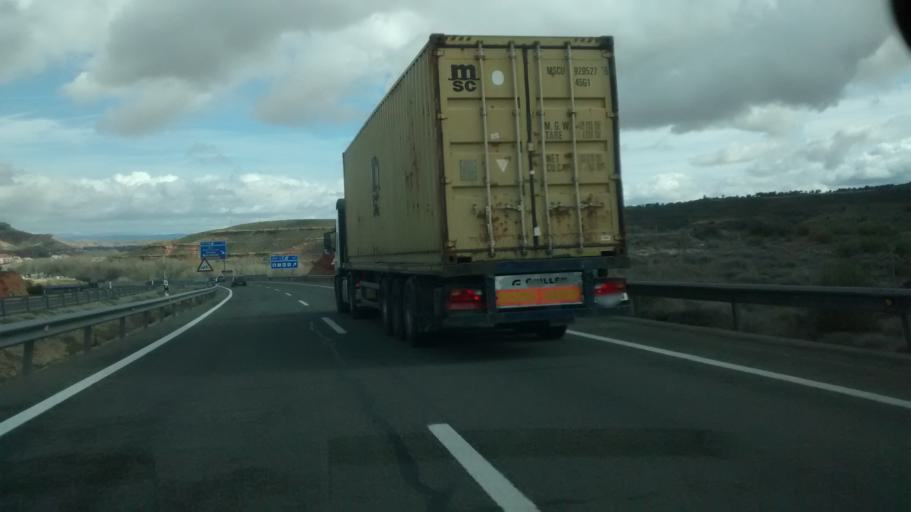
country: ES
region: Castille and Leon
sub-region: Provincia de Soria
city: Arcos de Jalon
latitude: 41.2042
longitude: -2.2968
